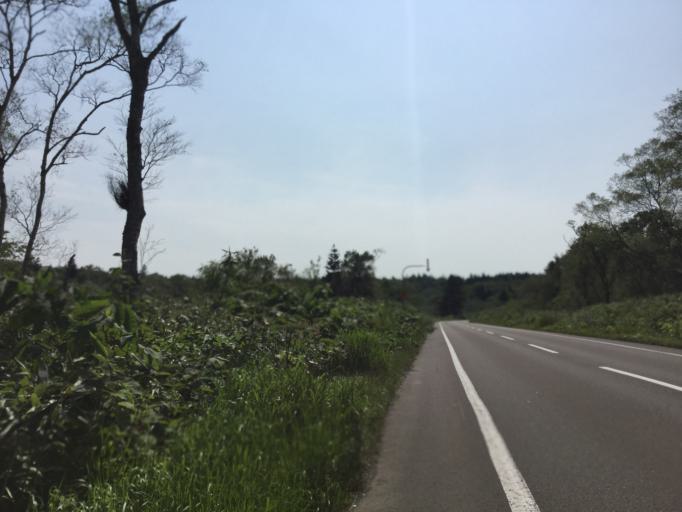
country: JP
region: Hokkaido
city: Makubetsu
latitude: 45.4068
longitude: 141.9951
